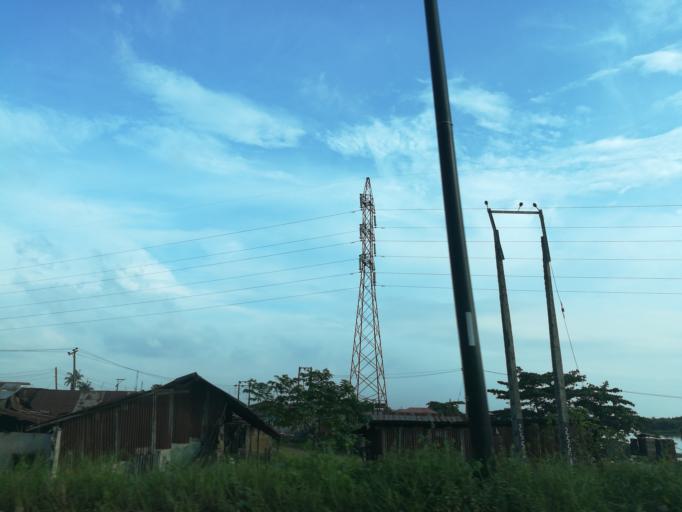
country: NG
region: Lagos
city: Ebute Ikorodu
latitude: 6.6192
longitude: 3.4697
